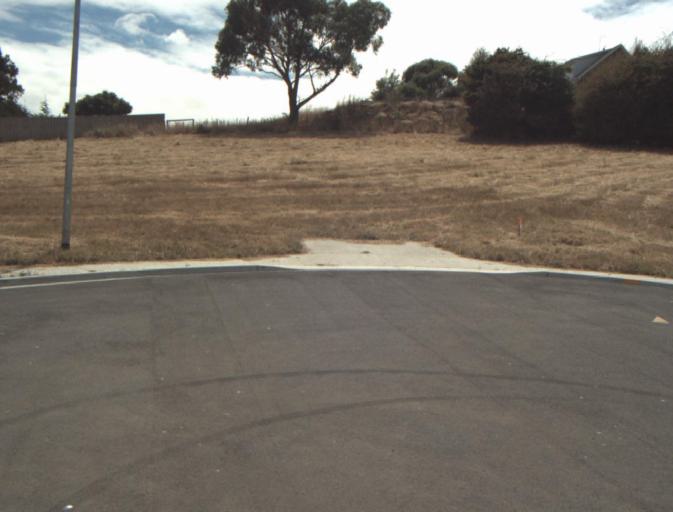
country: AU
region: Tasmania
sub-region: Launceston
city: Mayfield
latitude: -41.3804
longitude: 147.1137
